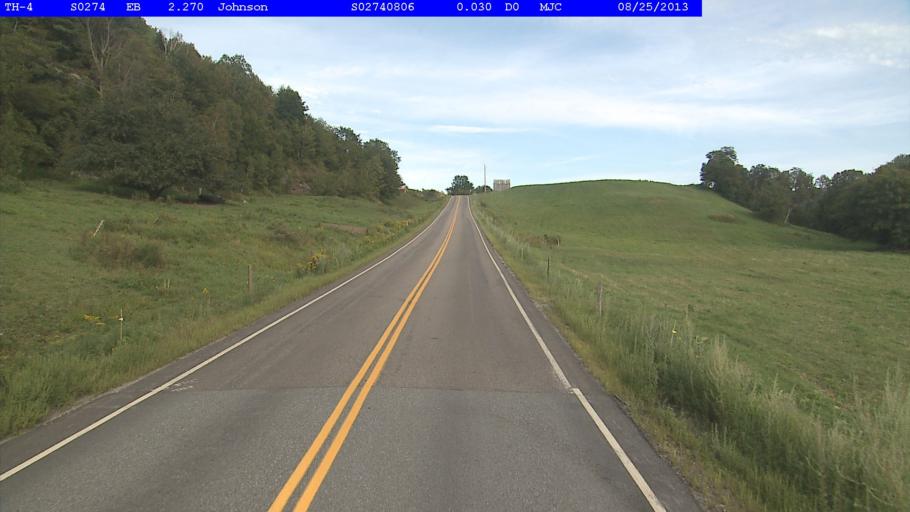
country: US
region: Vermont
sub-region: Lamoille County
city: Johnson
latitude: 44.6562
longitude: -72.7504
